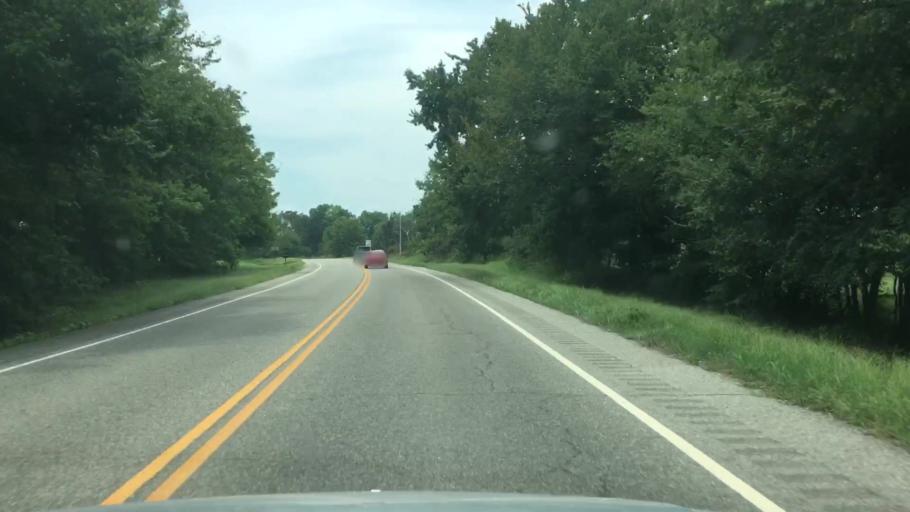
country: US
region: Oklahoma
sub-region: Muskogee County
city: Fort Gibson
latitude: 35.9362
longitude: -95.1622
